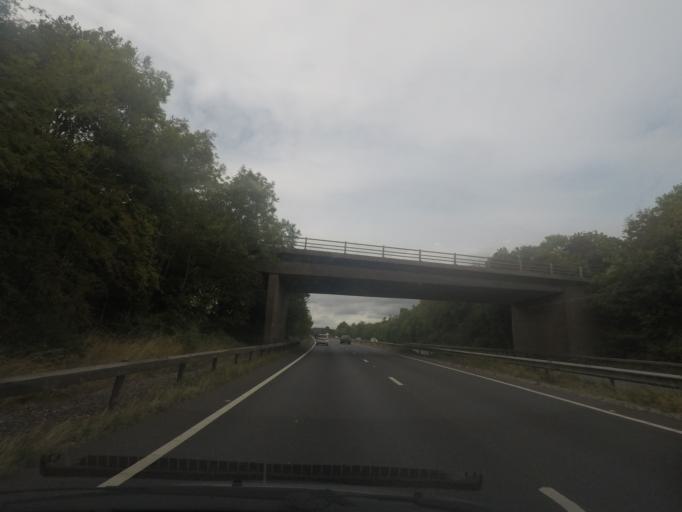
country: GB
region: England
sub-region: Hampshire
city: Overton
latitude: 51.2478
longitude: -1.3404
